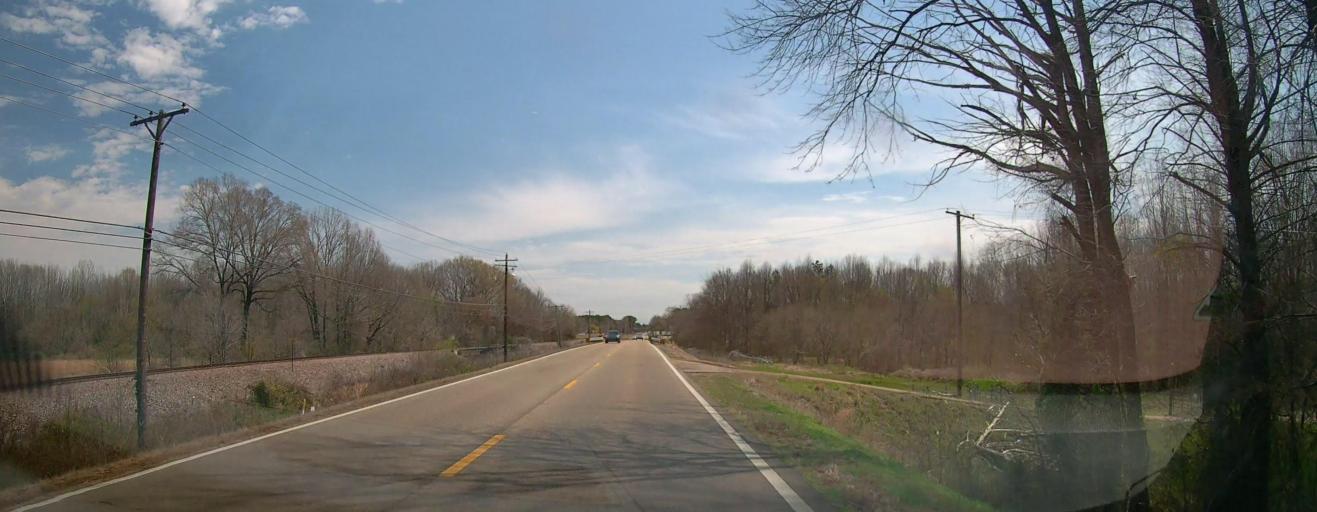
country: US
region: Mississippi
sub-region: Union County
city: New Albany
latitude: 34.5189
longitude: -89.0518
